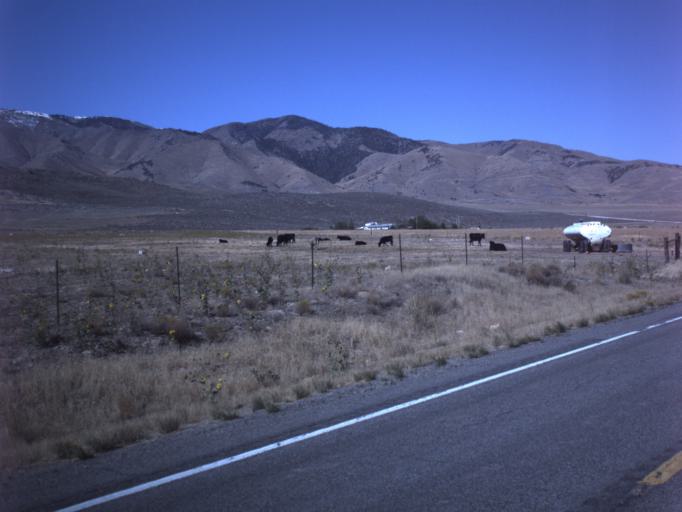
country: US
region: Utah
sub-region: Tooele County
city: Grantsville
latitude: 40.6335
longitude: -112.5164
